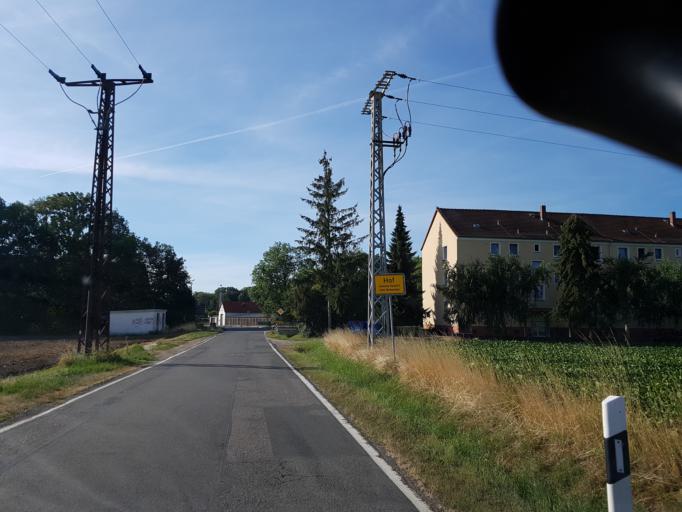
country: DE
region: Saxony
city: Stauchitz
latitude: 51.2432
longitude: 13.1885
